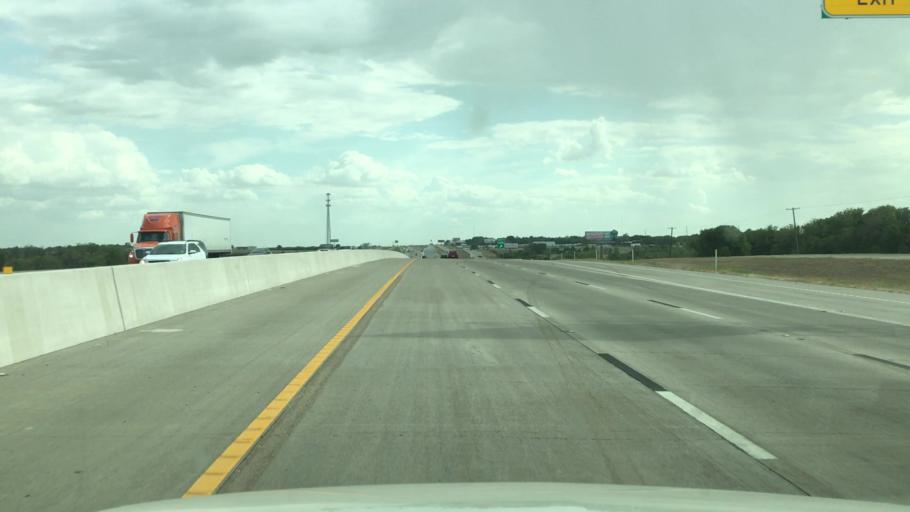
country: US
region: Texas
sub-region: McLennan County
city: Hewitt
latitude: 31.4432
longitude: -97.1814
